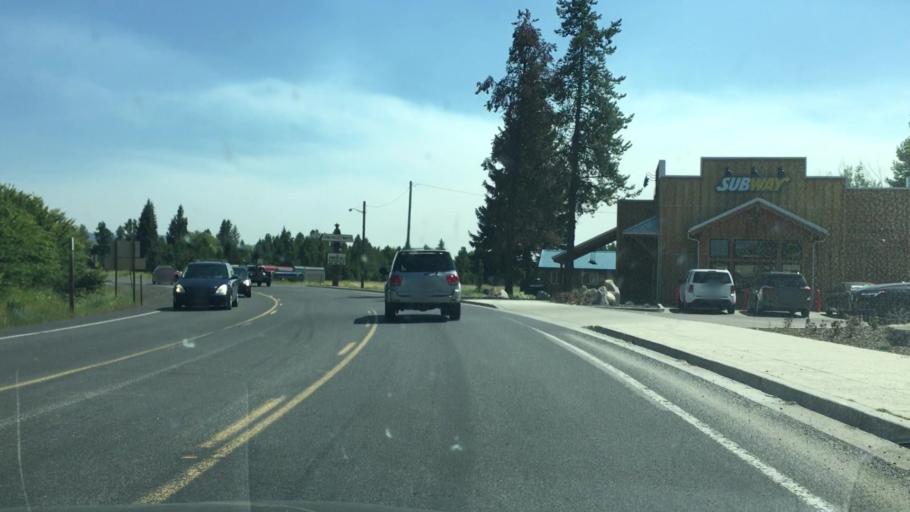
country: US
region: Idaho
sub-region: Valley County
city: McCall
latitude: 44.7308
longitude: -116.0783
